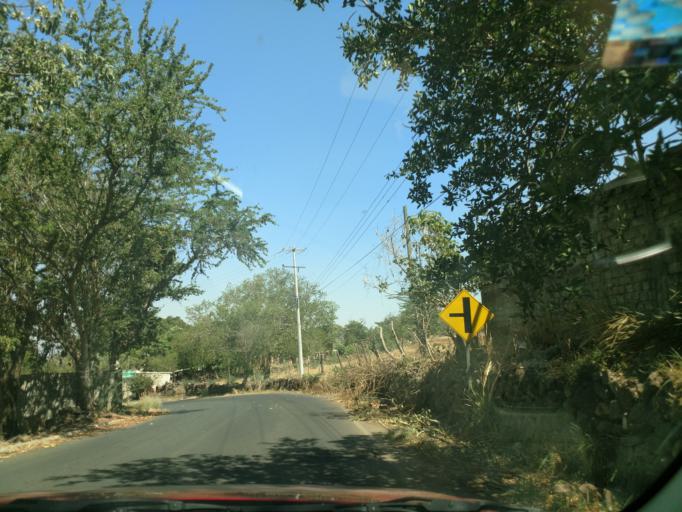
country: MX
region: Nayarit
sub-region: Tepic
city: La Corregidora
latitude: 21.4710
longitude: -104.6647
